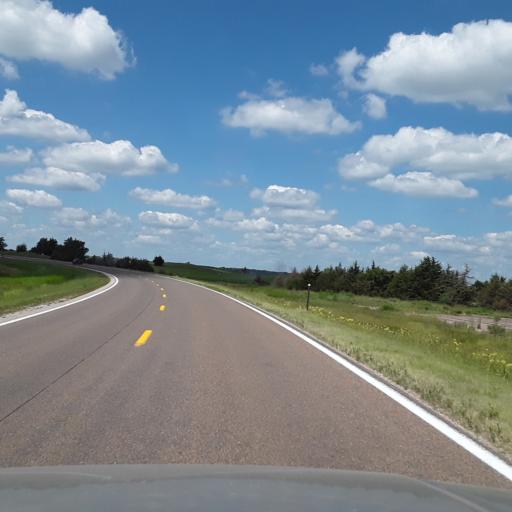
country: US
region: Nebraska
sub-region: Nance County
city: Genoa
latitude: 41.3970
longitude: -97.6947
